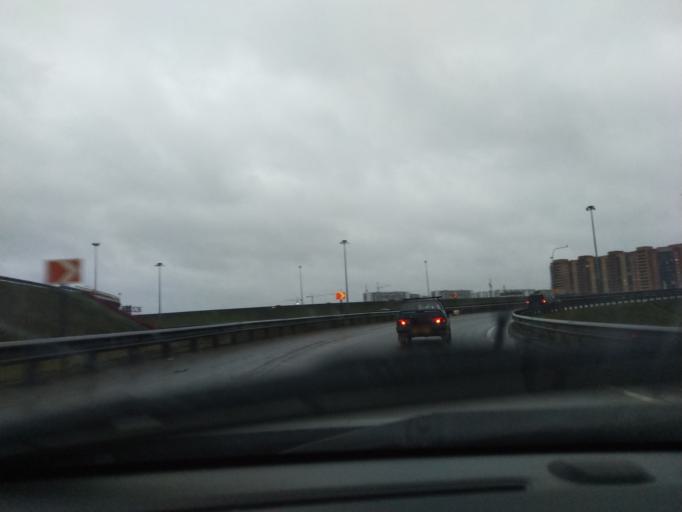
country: RU
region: St.-Petersburg
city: Sosnovaya Polyana
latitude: 59.8007
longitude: 30.1604
